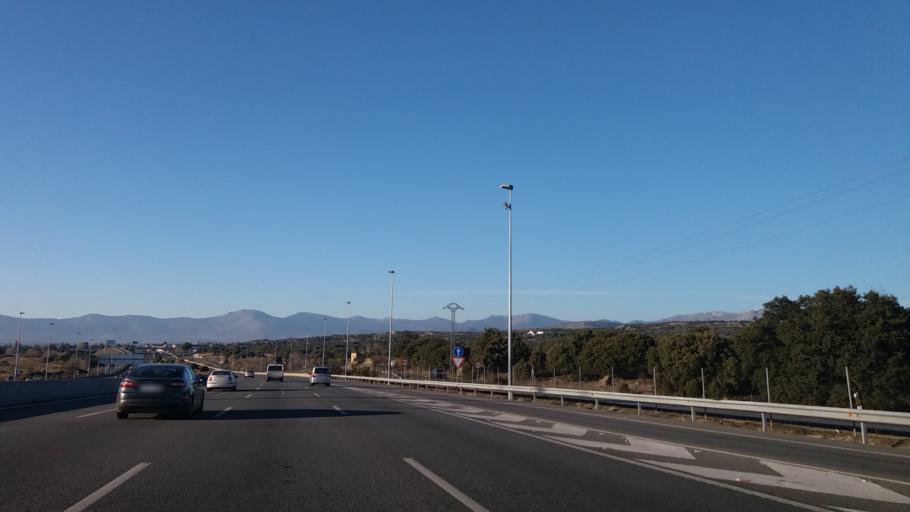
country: ES
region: Madrid
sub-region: Provincia de Madrid
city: Collado-Villalba
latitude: 40.6154
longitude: -3.9812
